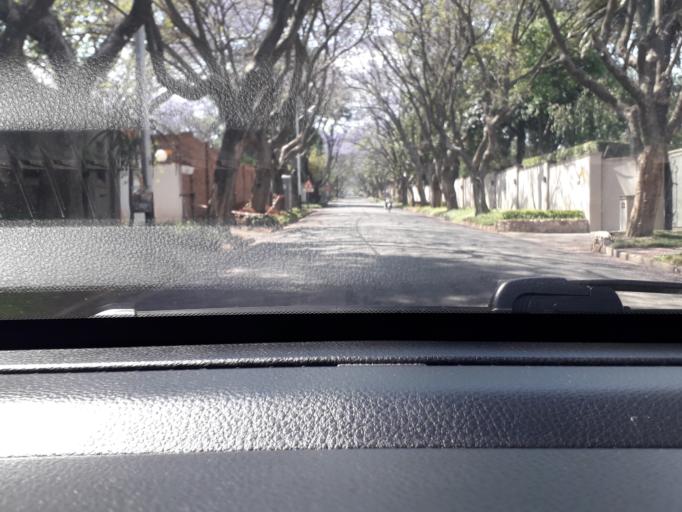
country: ZA
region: Gauteng
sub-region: City of Johannesburg Metropolitan Municipality
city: Johannesburg
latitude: -26.1425
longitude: 28.0478
